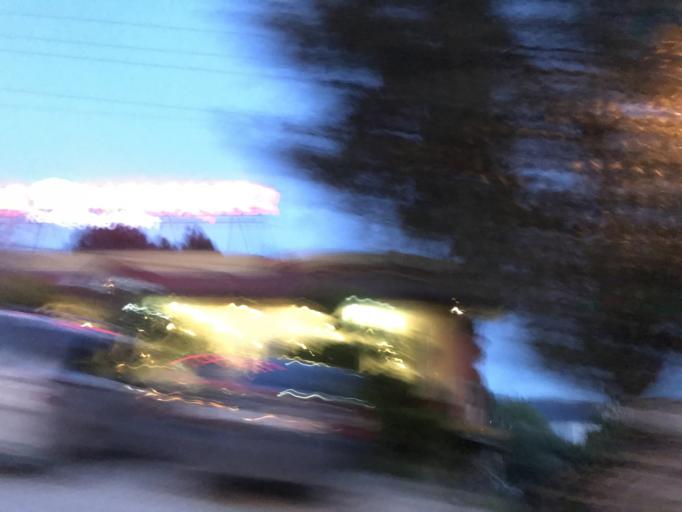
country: TR
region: Hatay
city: Karacay
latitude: 36.1551
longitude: 36.0951
